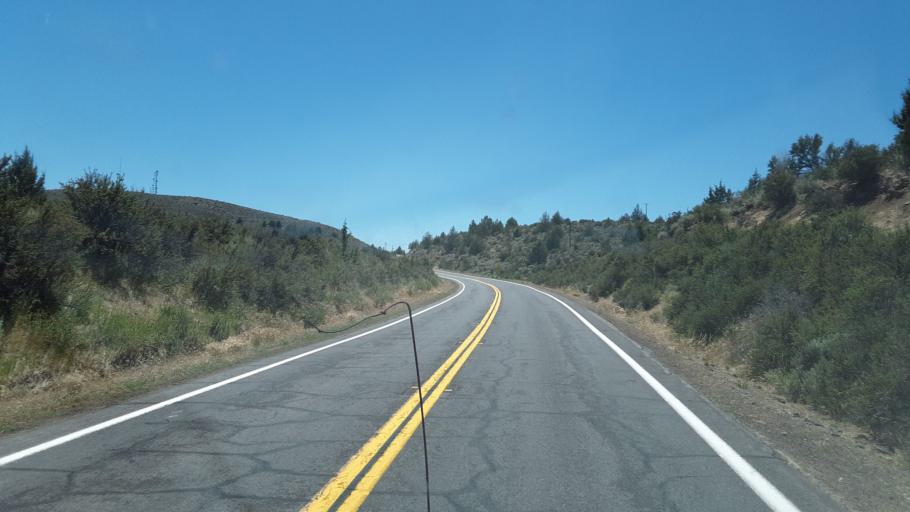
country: US
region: California
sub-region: Lassen County
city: Johnstonville
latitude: 40.4657
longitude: -120.5664
